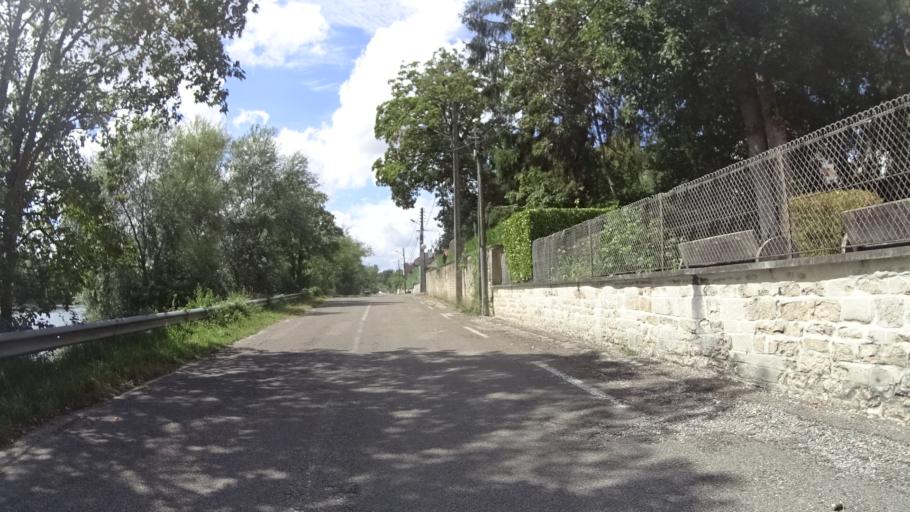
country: FR
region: Franche-Comte
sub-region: Departement du Jura
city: Dole
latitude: 47.0856
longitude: 5.4868
